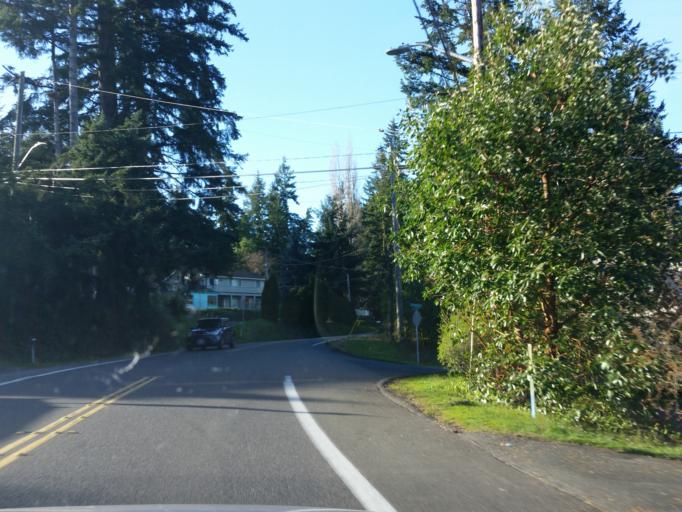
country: US
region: Washington
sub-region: Snohomish County
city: Mountlake Terrace
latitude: 47.7666
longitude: -122.3159
